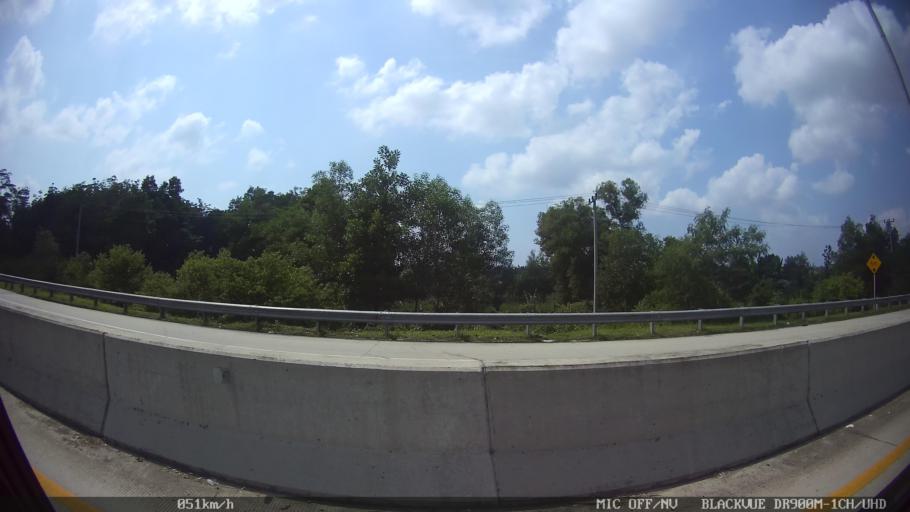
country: ID
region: Lampung
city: Natar
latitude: -5.2786
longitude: 105.2091
